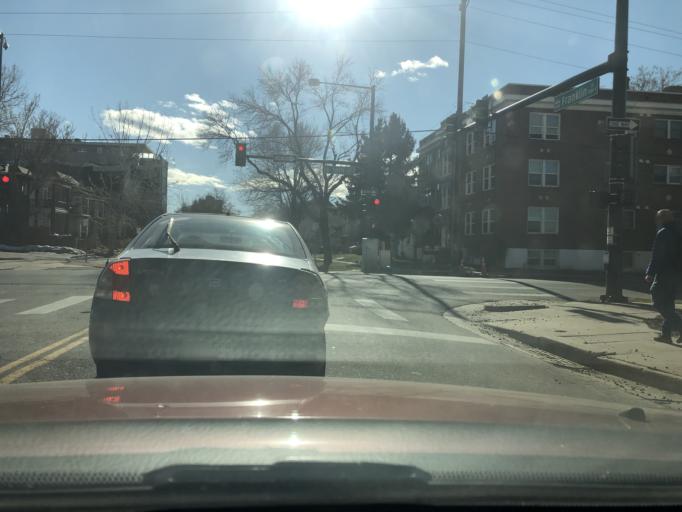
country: US
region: Colorado
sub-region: Denver County
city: Denver
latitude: 39.7450
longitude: -104.9685
